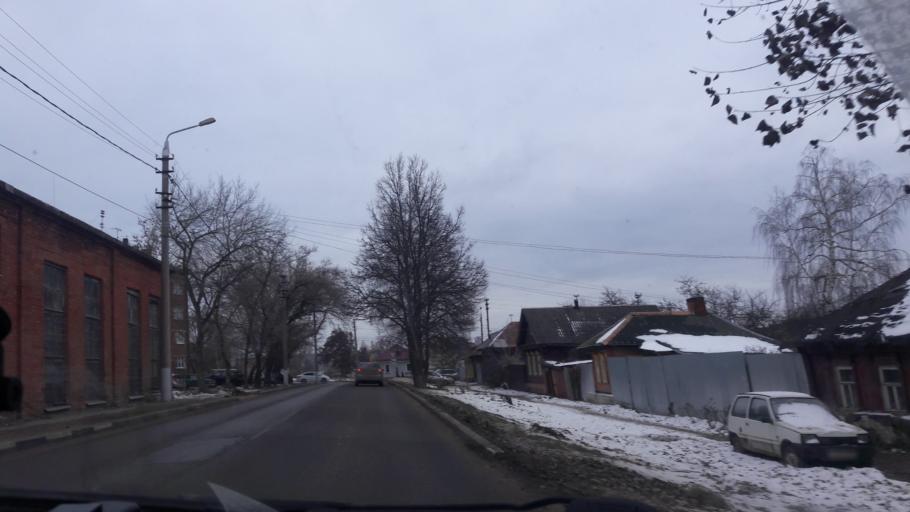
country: RU
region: Tula
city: Tula
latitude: 54.2048
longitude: 37.6580
